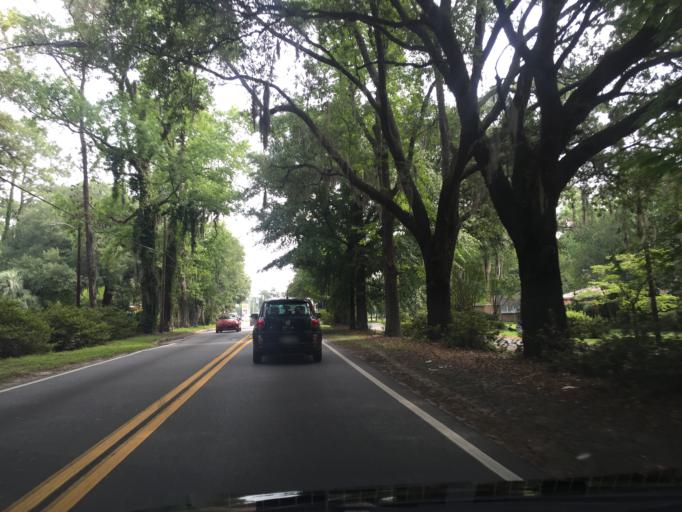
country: US
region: Georgia
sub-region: Chatham County
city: Thunderbolt
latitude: 32.0230
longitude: -81.0952
